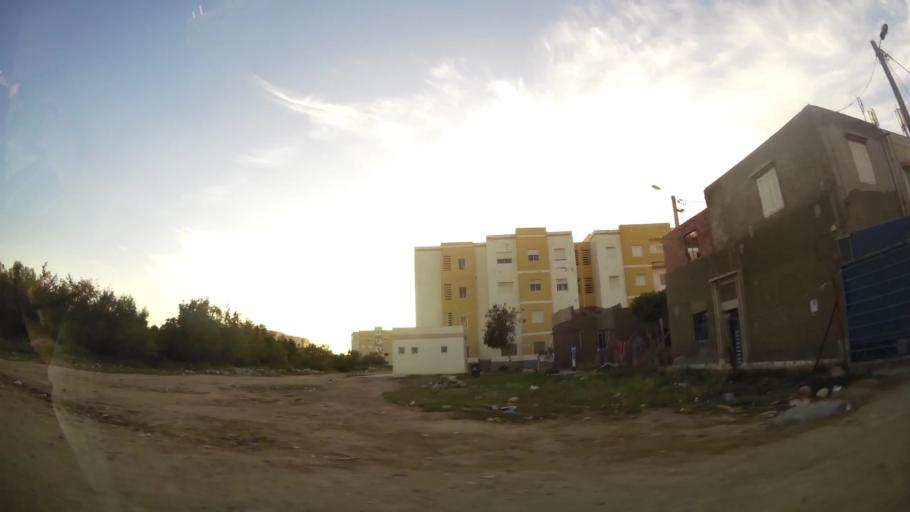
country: MA
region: Oriental
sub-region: Berkane-Taourirt
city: Madagh
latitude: 35.0785
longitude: -2.2349
